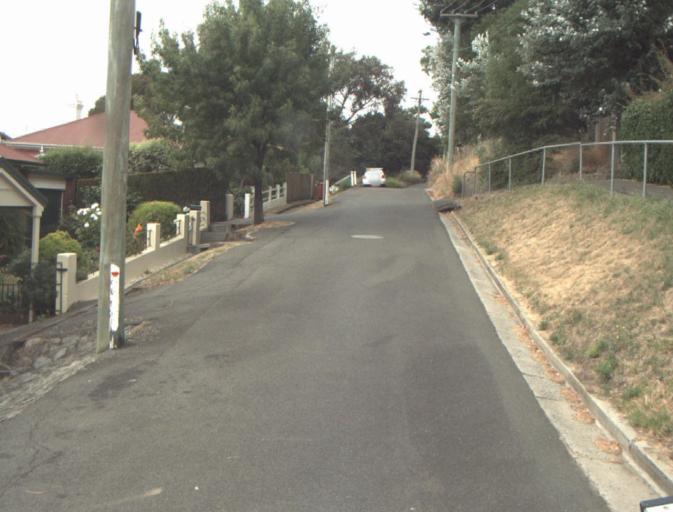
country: AU
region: Tasmania
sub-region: Launceston
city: East Launceston
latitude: -41.4409
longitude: 147.1489
